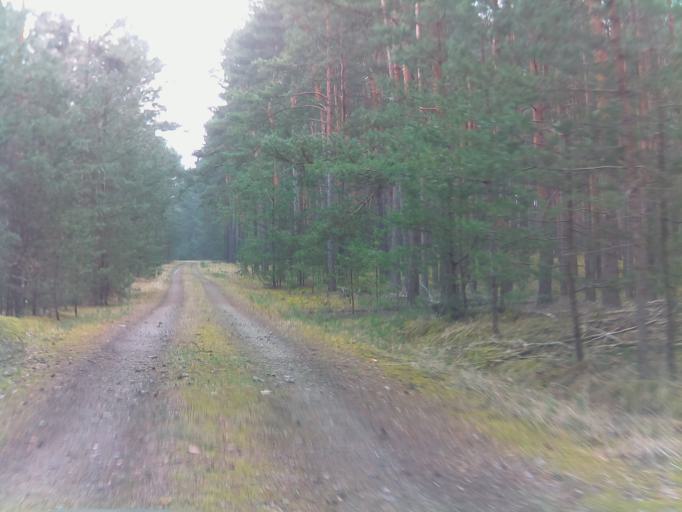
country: DE
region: Brandenburg
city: Kasel-Golzig
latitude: 52.0171
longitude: 13.7104
